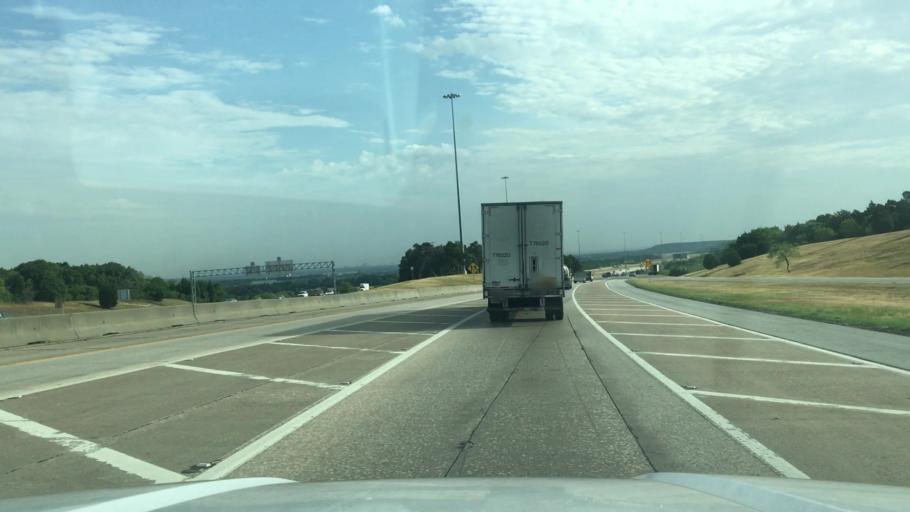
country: US
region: Texas
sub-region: Dallas County
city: Duncanville
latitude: 32.6763
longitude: -96.9461
